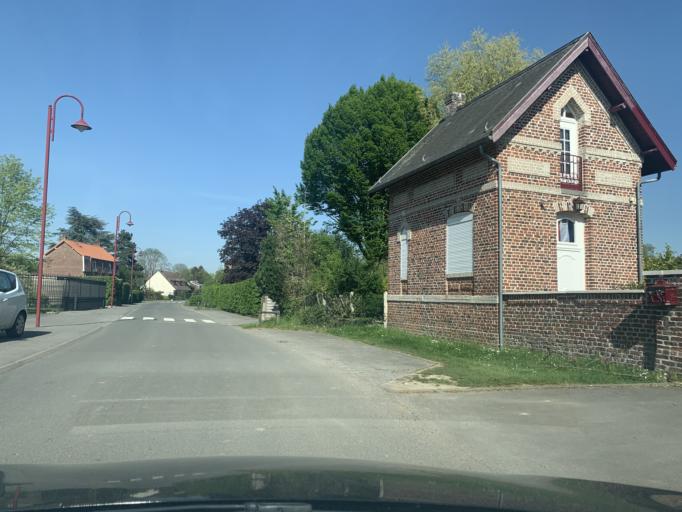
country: FR
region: Nord-Pas-de-Calais
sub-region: Departement du Nord
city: Proville
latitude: 50.1671
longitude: 3.2106
